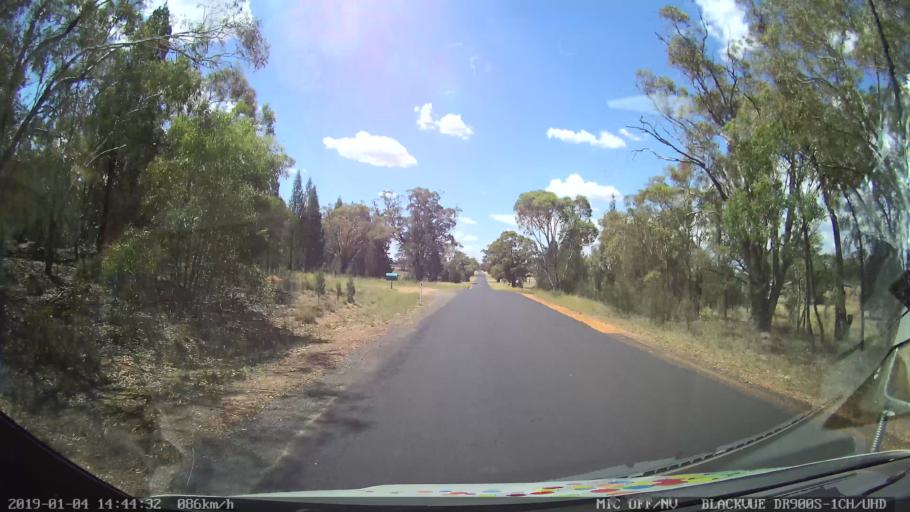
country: AU
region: New South Wales
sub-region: Dubbo Municipality
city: Dubbo
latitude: -32.1050
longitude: 148.6558
